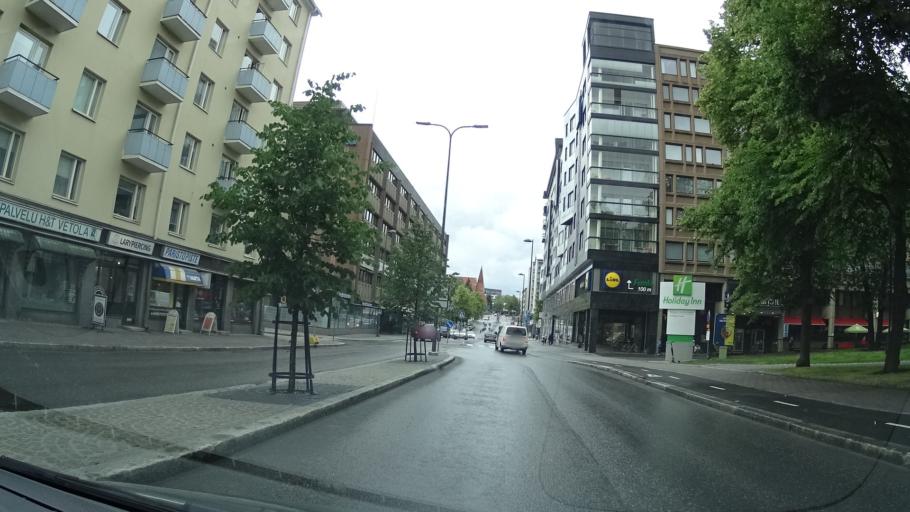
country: FI
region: Pirkanmaa
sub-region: Tampere
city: Tampere
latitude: 61.4993
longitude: 23.7717
